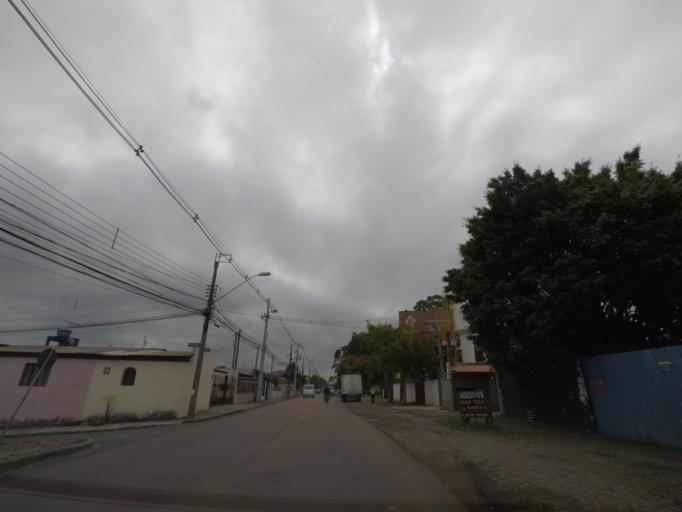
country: BR
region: Parana
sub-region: Curitiba
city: Curitiba
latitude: -25.4991
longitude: -49.3350
